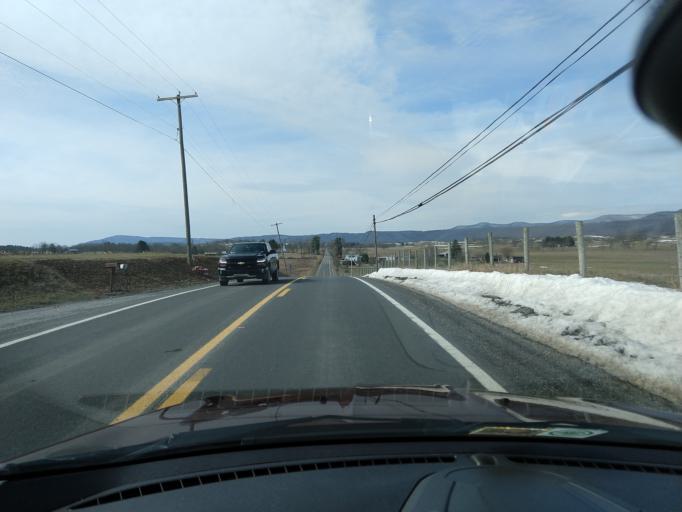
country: US
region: West Virginia
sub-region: Pocahontas County
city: Marlinton
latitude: 38.1503
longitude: -80.1886
